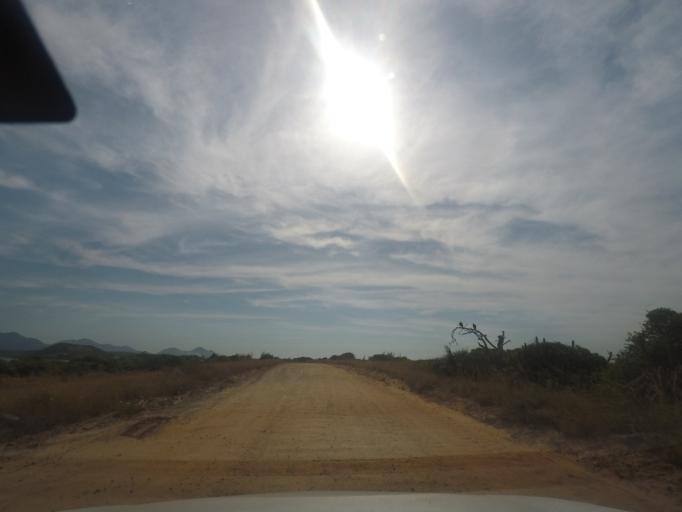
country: BR
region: Rio de Janeiro
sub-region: Marica
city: Marica
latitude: -22.9605
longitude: -42.8417
